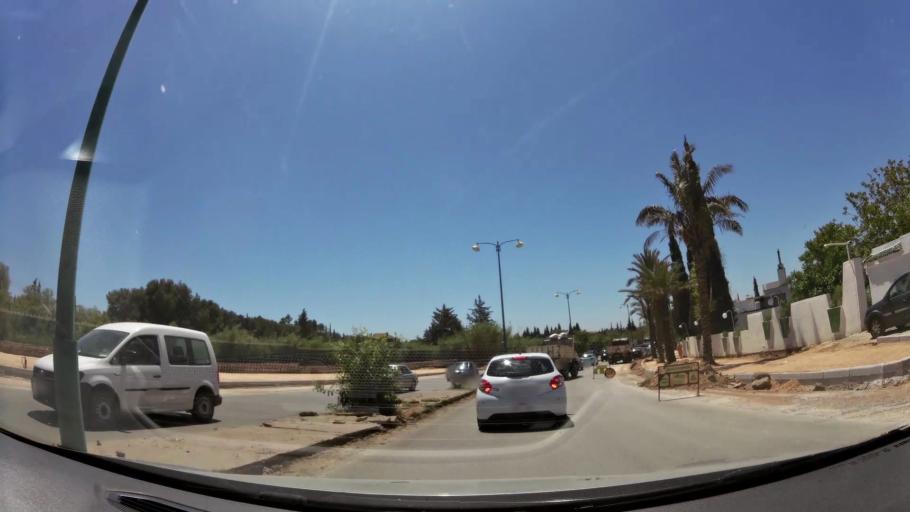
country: MA
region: Meknes-Tafilalet
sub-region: Meknes
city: Meknes
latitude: 33.8815
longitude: -5.5335
